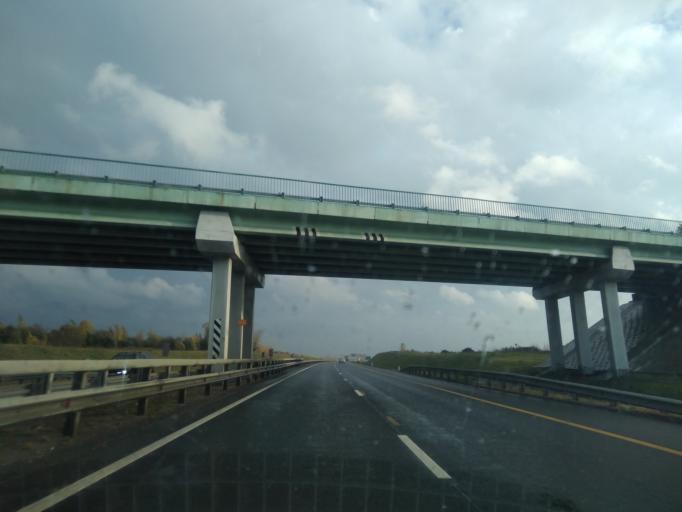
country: RU
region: Lipetsk
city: Yelets
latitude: 52.5636
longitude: 38.7103
